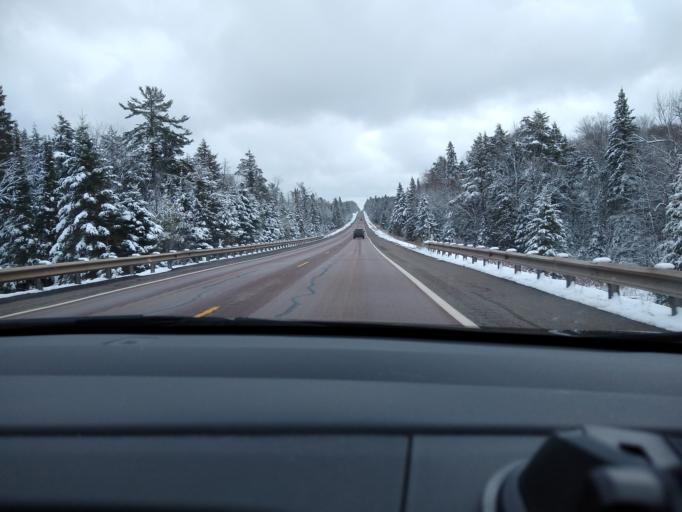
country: US
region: Wisconsin
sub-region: Vilas County
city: Eagle River
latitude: 46.2275
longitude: -89.0707
